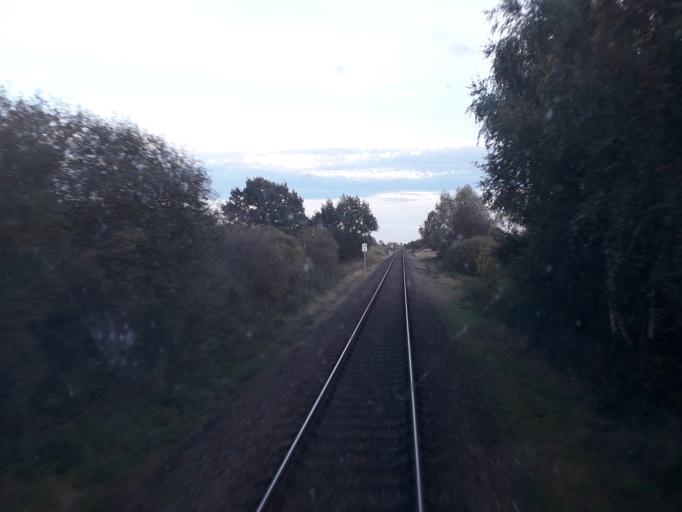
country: DE
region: Brandenburg
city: Walsleben
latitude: 52.9438
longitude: 12.6893
